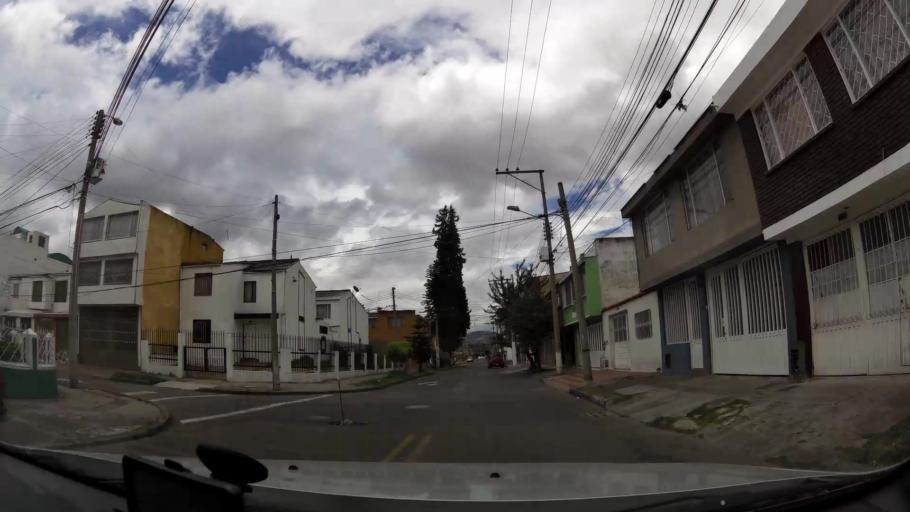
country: CO
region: Bogota D.C.
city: Bogota
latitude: 4.6069
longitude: -74.1114
